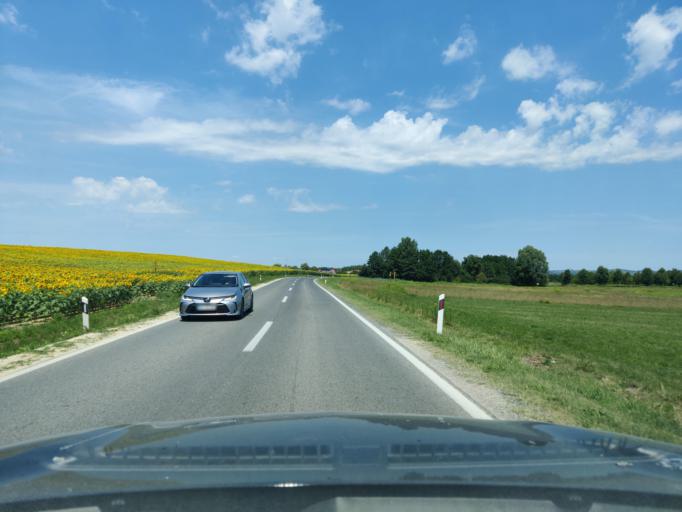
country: HR
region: Medimurska
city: Vratisinec
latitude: 46.4868
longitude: 16.4256
